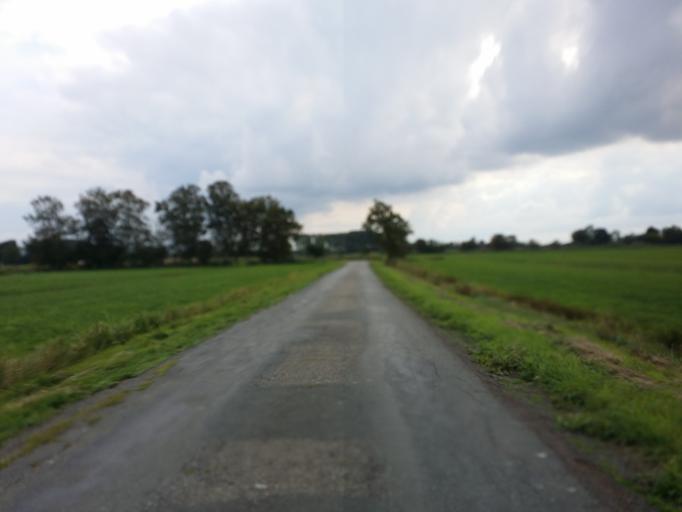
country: DE
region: Lower Saxony
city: Oederquart
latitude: 53.7796
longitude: 9.2176
